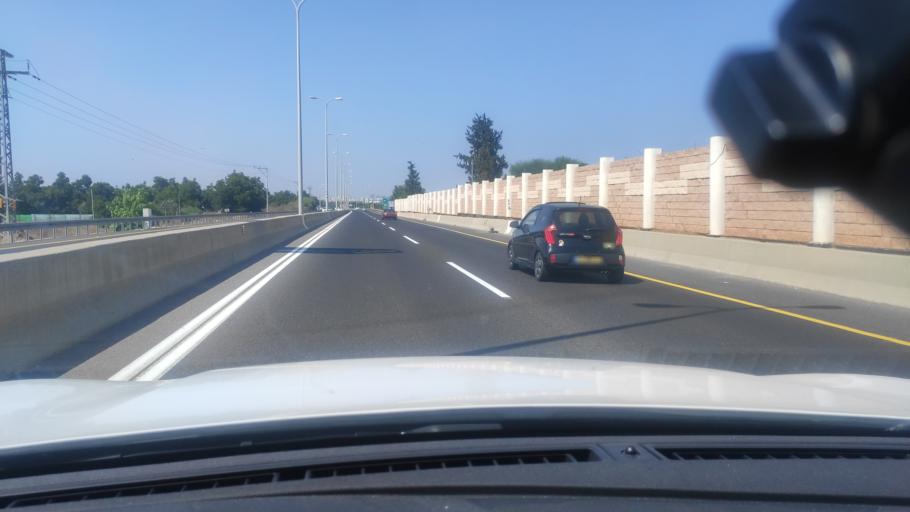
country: IL
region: Central District
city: Kfar Saba
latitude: 32.1553
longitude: 34.9244
